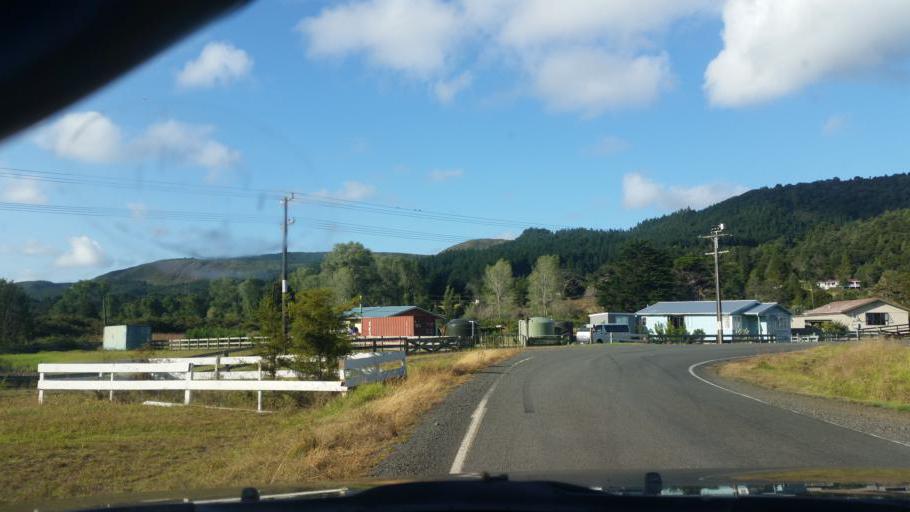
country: NZ
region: Northland
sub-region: Kaipara District
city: Dargaville
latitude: -35.7683
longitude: 173.7003
